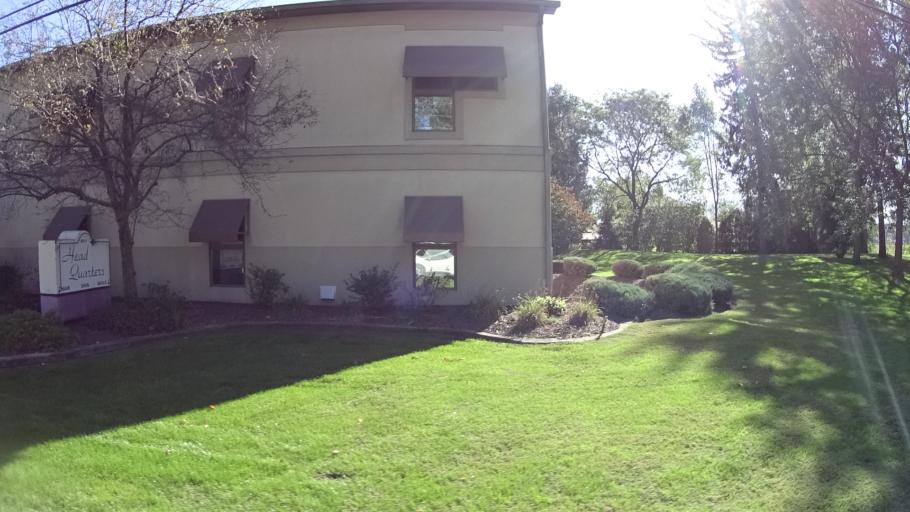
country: US
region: Ohio
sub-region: Lorain County
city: Lorain
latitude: 41.4169
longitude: -82.1616
